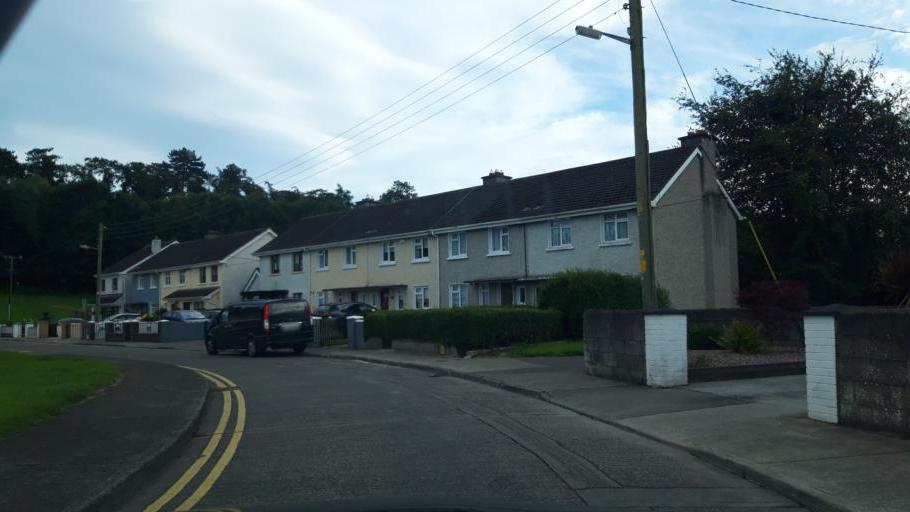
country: IE
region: Leinster
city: Lucan
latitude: 53.3581
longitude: -6.4453
